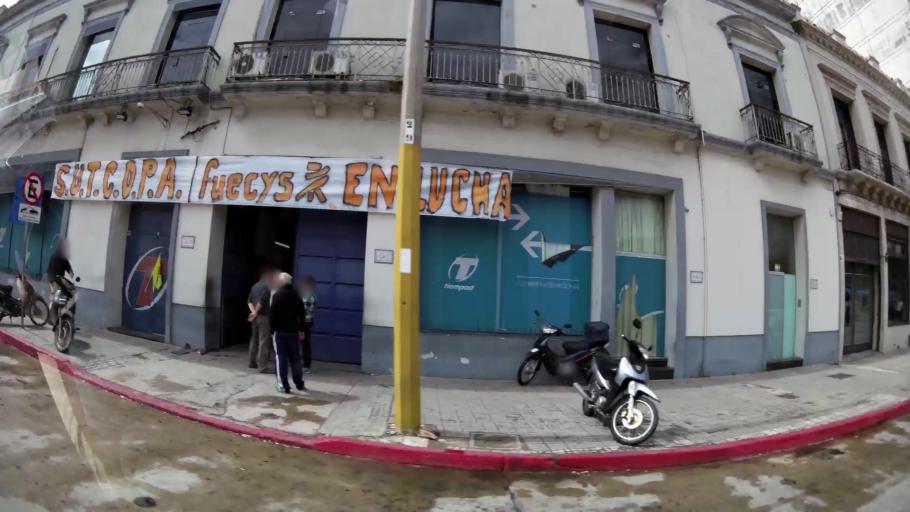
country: UY
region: Montevideo
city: Montevideo
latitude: -34.9046
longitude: -56.2099
